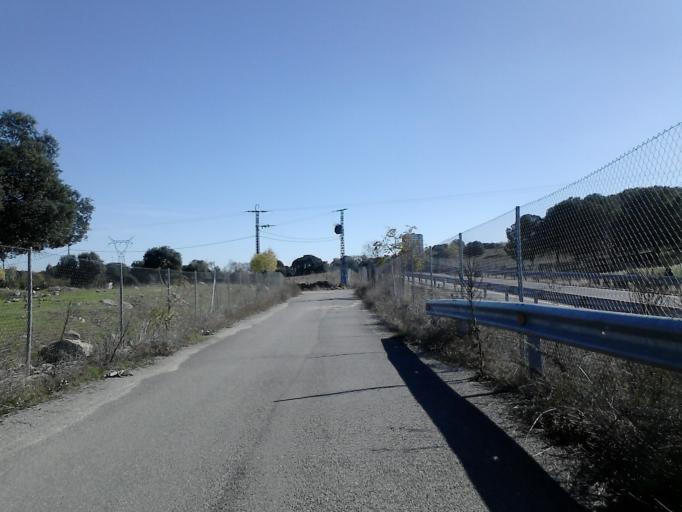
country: ES
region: Madrid
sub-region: Provincia de Madrid
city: Galapagar
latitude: 40.5747
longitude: -3.9867
